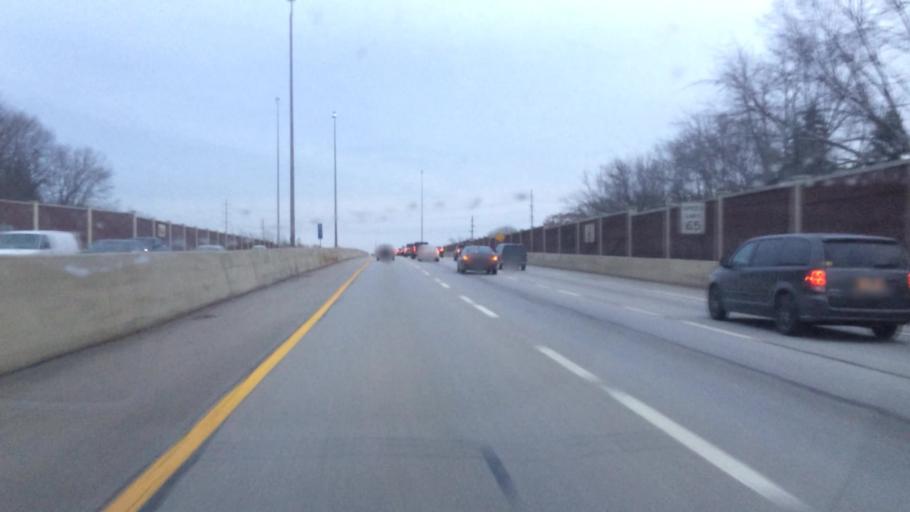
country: US
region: Ohio
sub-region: Summit County
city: Fairlawn
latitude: 41.1067
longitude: -81.5995
